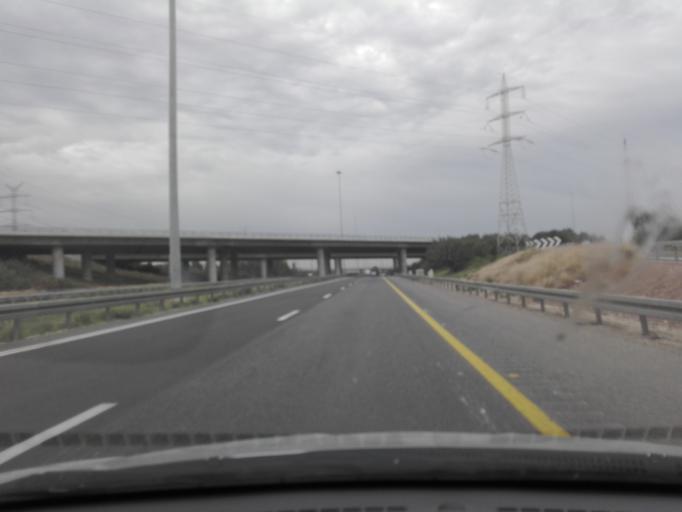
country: IL
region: Central District
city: Lod
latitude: 31.9118
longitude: 34.8985
